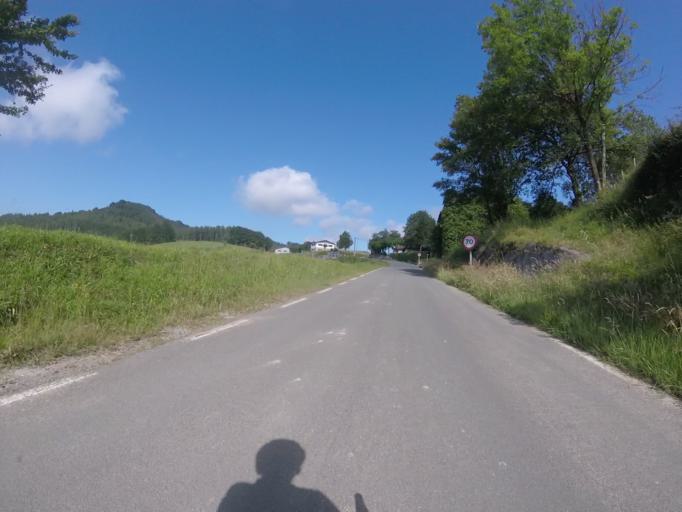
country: ES
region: Basque Country
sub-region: Provincia de Guipuzcoa
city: Ormaiztegui
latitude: 43.0865
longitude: -2.2437
